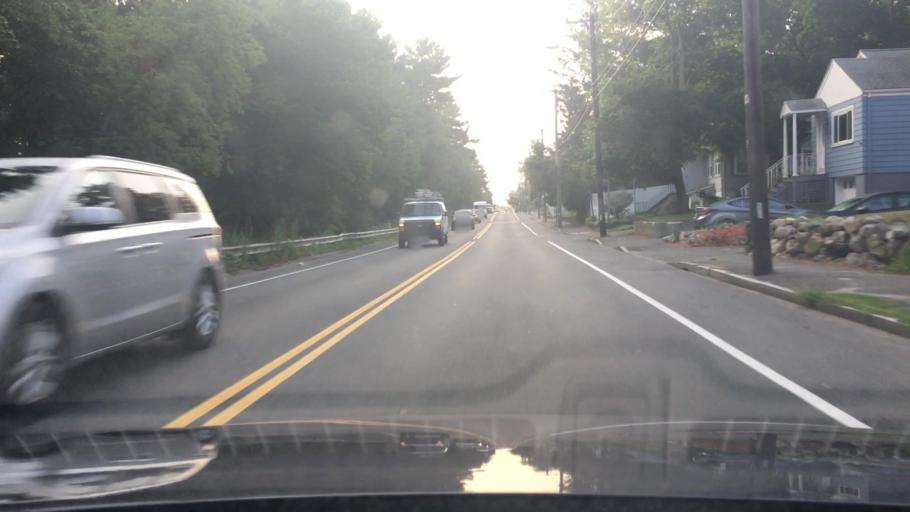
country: US
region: Massachusetts
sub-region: Essex County
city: Saugus
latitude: 42.4759
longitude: -70.9987
